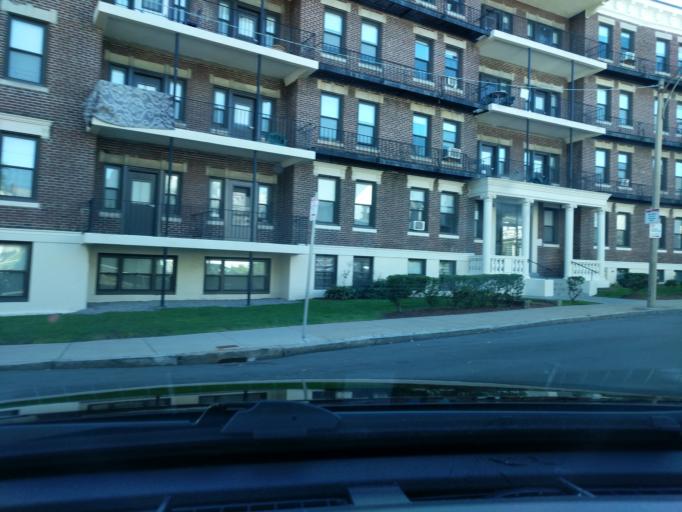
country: US
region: Massachusetts
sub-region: Norfolk County
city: Brookline
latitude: 42.3491
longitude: -71.1358
